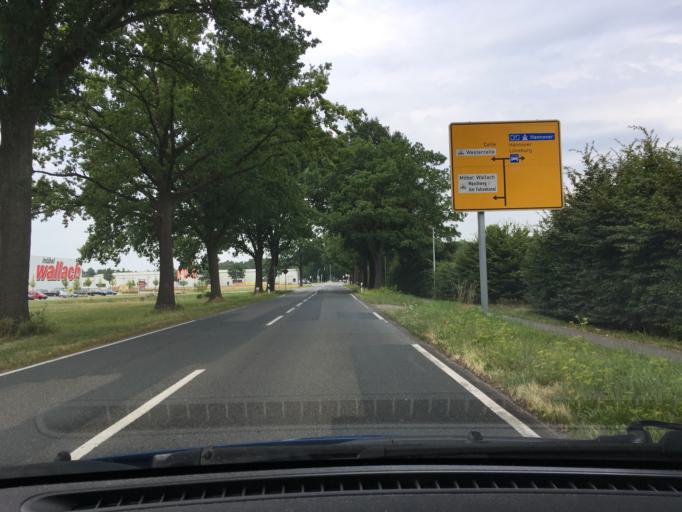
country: DE
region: Lower Saxony
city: Adelheidsdorf
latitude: 52.5820
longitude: 10.0651
